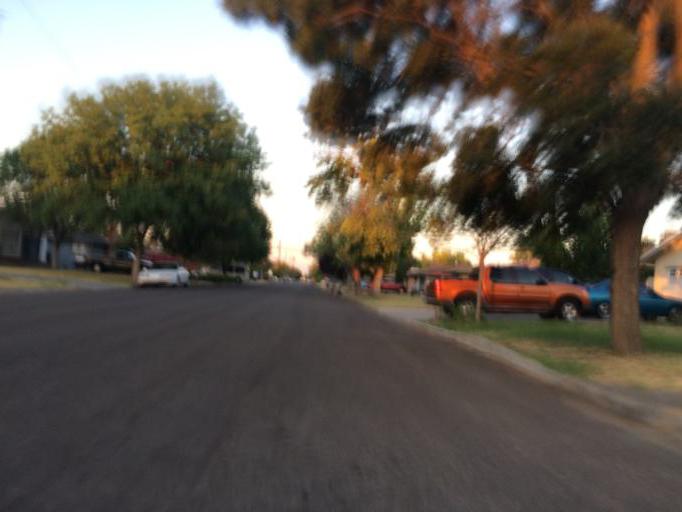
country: US
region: California
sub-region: Fresno County
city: Fresno
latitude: 36.7759
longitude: -119.7424
